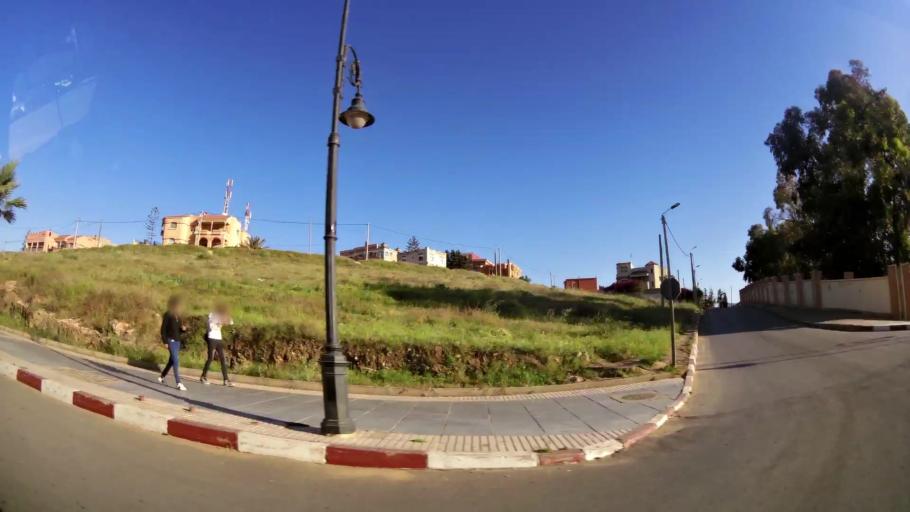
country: MA
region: Oriental
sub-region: Berkane-Taourirt
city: Berkane
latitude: 34.9287
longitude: -2.3230
